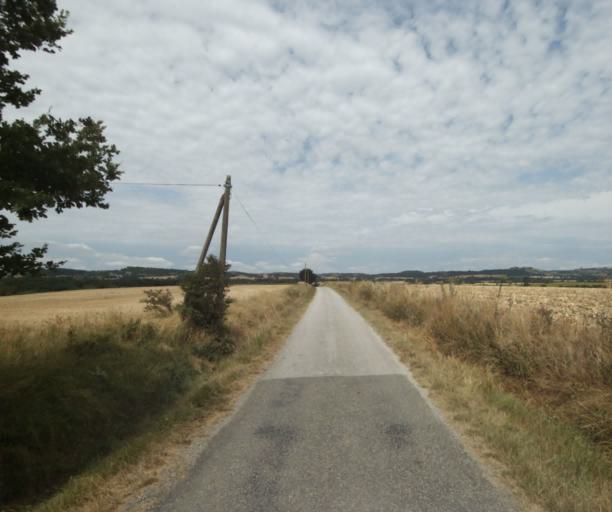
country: FR
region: Midi-Pyrenees
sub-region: Departement de la Haute-Garonne
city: Saint-Felix-Lauragais
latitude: 43.4031
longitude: 1.9031
